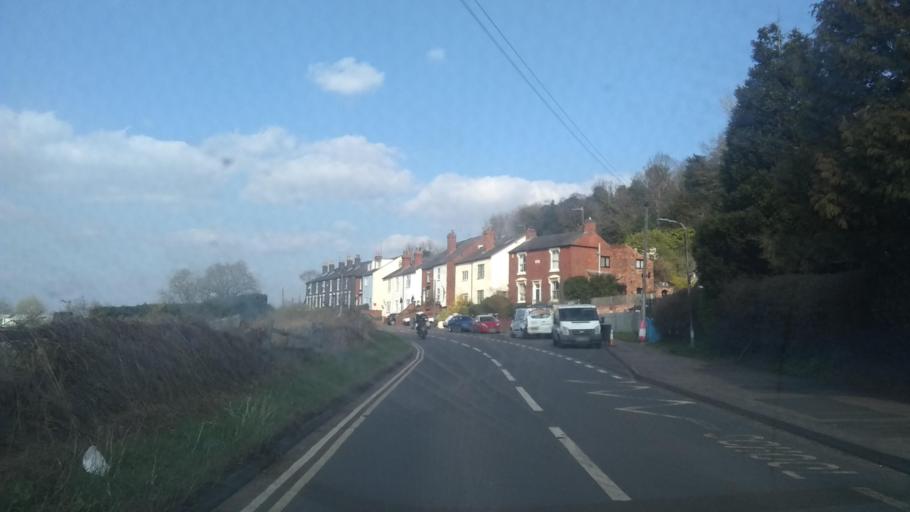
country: GB
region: England
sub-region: Worcestershire
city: Stourport-on-Severn
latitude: 52.3480
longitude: -2.2599
